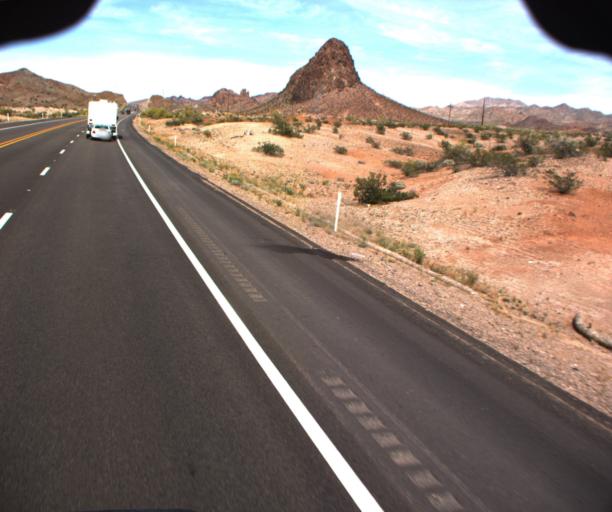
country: US
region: Arizona
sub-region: Mohave County
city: Desert Hills
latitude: 34.6054
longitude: -114.3620
